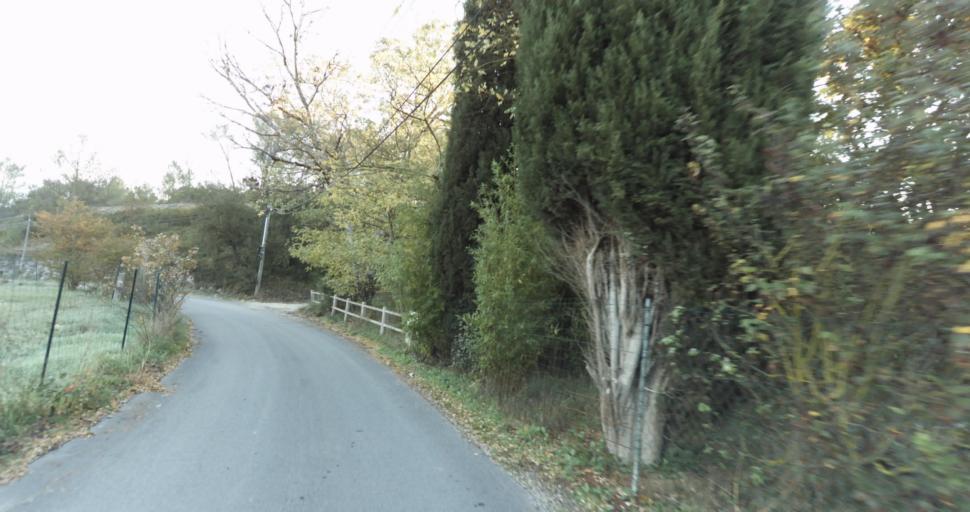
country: FR
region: Provence-Alpes-Cote d'Azur
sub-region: Departement des Bouches-du-Rhone
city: Venelles
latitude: 43.5858
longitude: 5.5070
